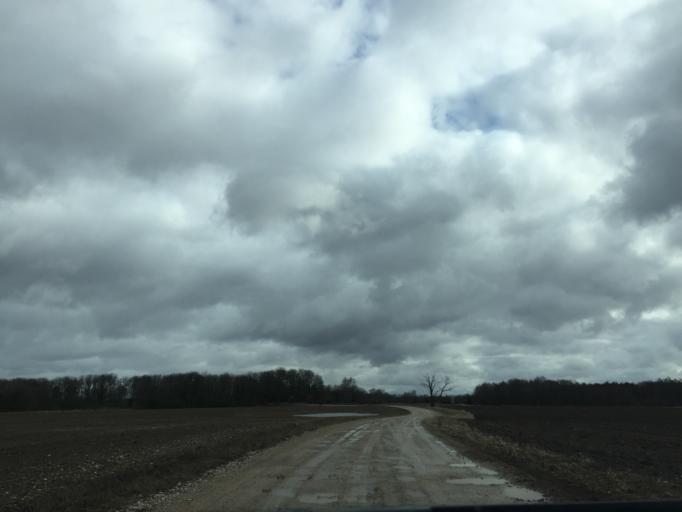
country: EE
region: Laeaene
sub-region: Ridala Parish
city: Uuemoisa
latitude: 58.6904
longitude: 23.5564
